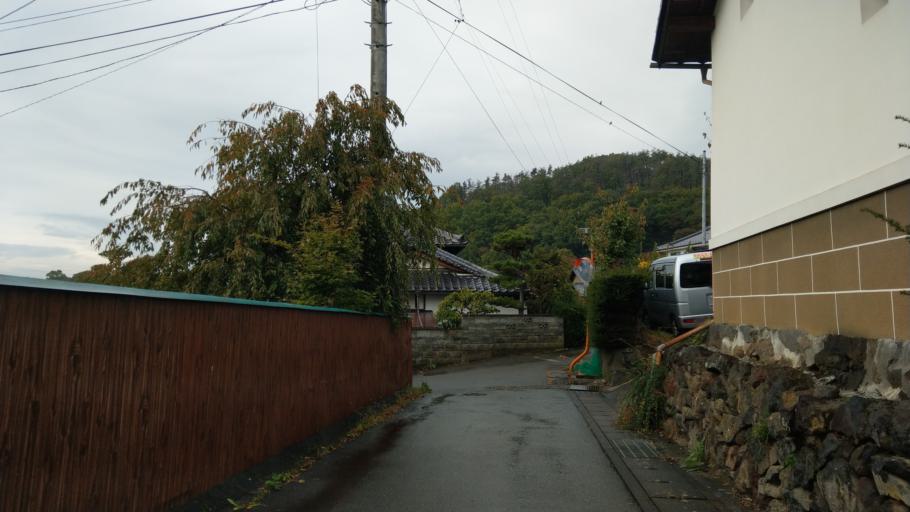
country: JP
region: Nagano
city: Komoro
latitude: 36.3415
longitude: 138.4171
